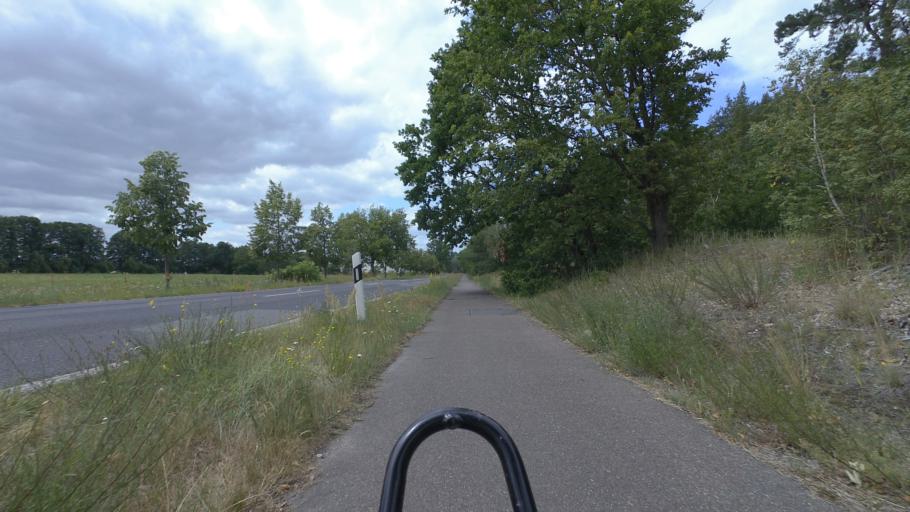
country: DE
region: Brandenburg
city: Trebbin
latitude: 52.2376
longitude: 13.1795
